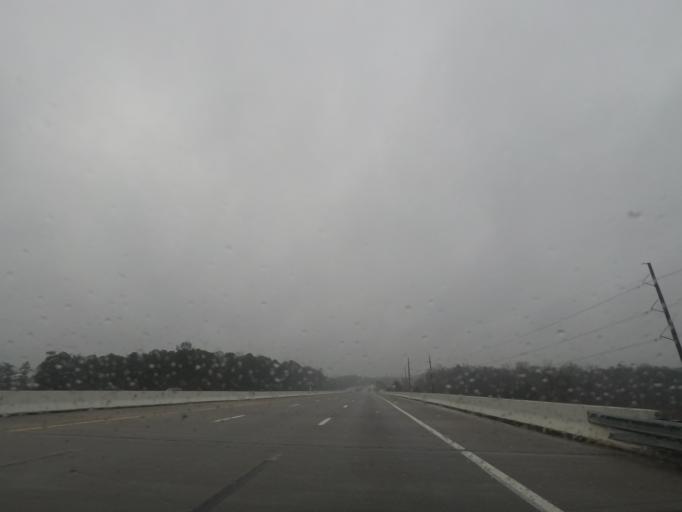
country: US
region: North Carolina
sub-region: Wake County
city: Green Level
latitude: 35.7787
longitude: -78.8858
